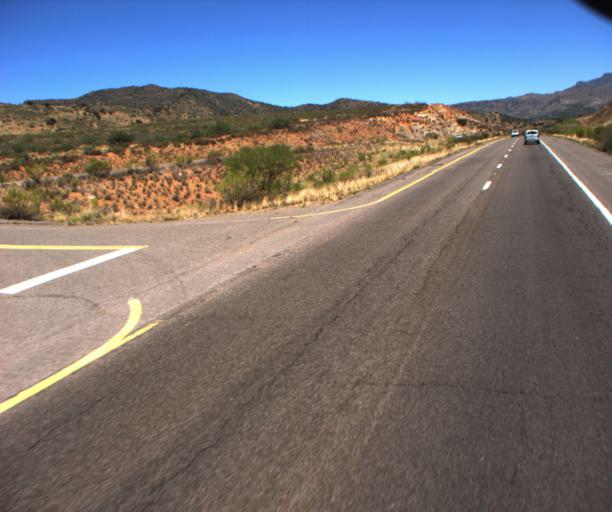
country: US
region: Arizona
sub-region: Gila County
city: Tonto Basin
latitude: 33.8553
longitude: -111.4720
